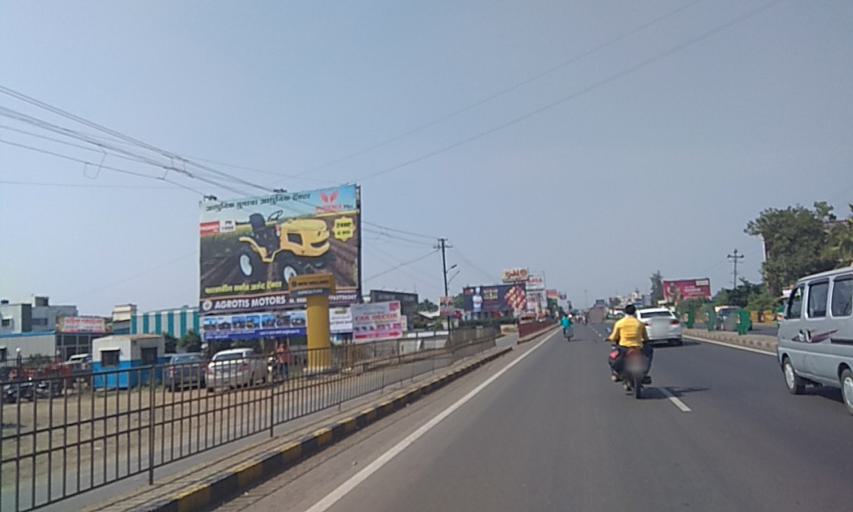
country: IN
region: Maharashtra
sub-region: Pune Division
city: Lohogaon
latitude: 18.4914
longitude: 74.0057
